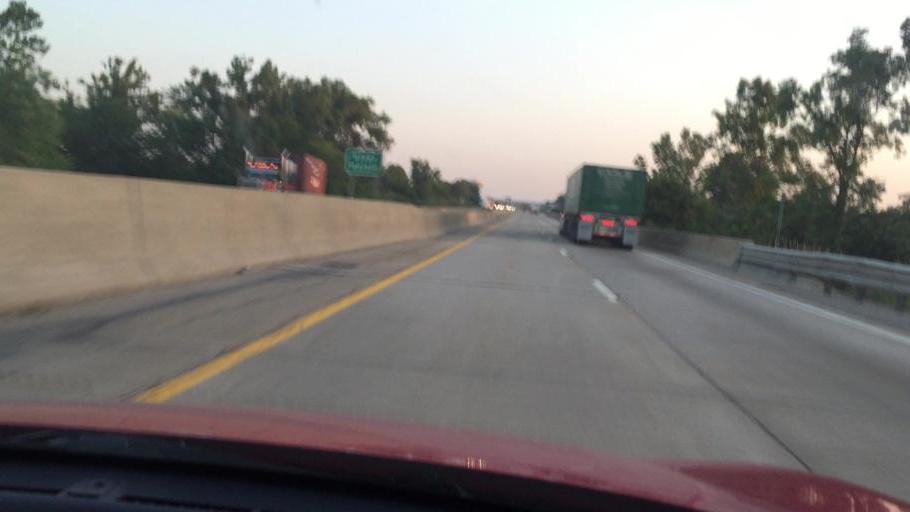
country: US
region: Michigan
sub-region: Monroe County
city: Dundee
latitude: 41.9454
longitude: -83.6656
